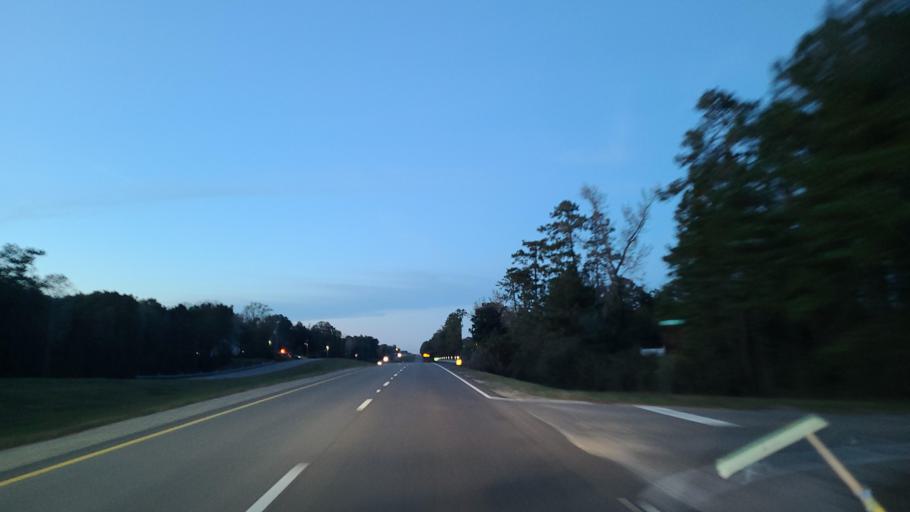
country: US
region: Mississippi
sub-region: Forrest County
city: Hattiesburg
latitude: 31.2083
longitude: -89.2604
